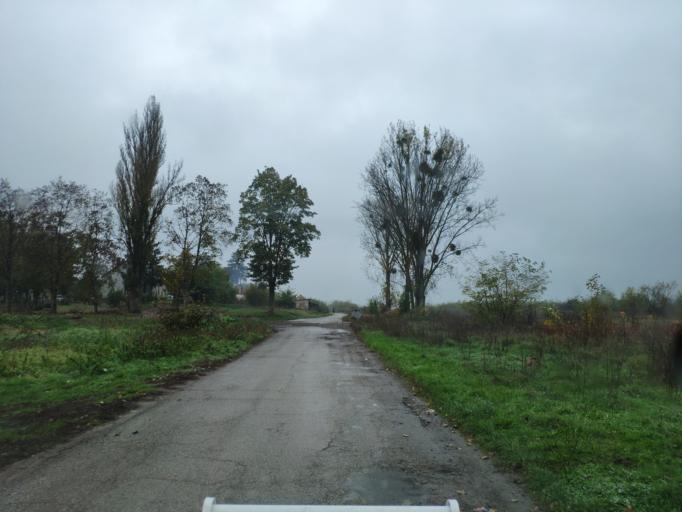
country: SK
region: Kosicky
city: Cierna nad Tisou
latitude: 48.4418
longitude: 21.9999
